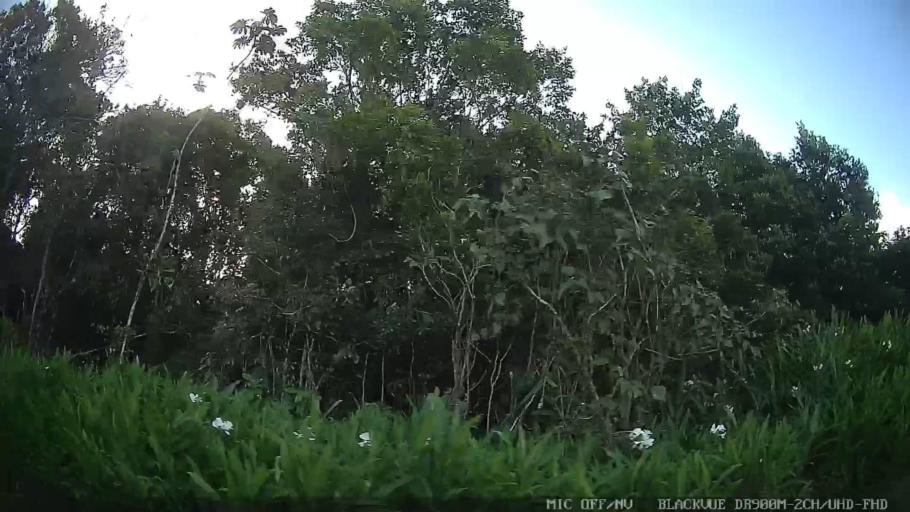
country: BR
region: Sao Paulo
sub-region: Itanhaem
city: Itanhaem
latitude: -24.1380
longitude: -46.7194
